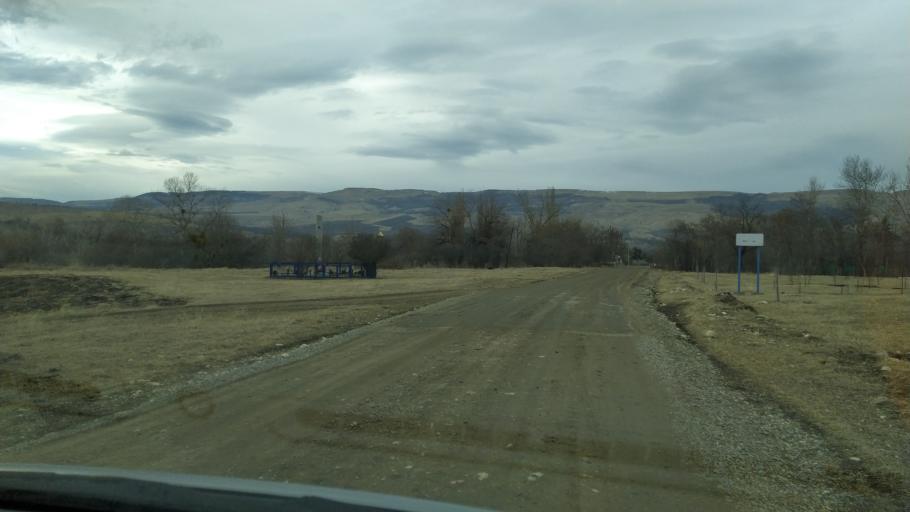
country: RU
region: Krasnodarskiy
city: Peredovaya
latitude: 44.0848
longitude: 41.3648
